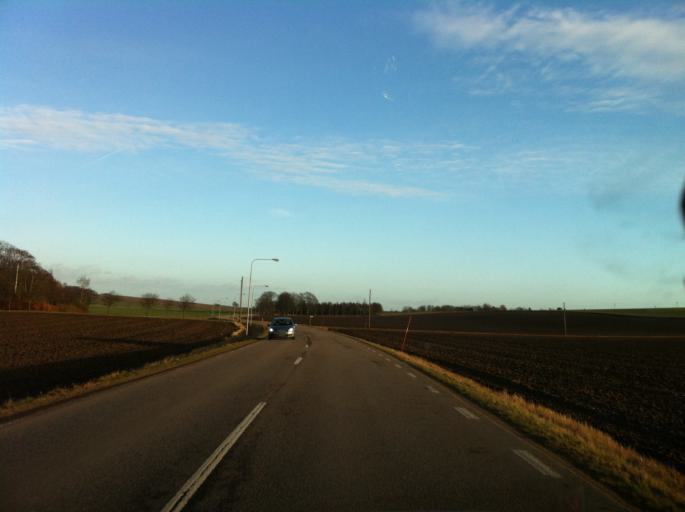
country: SE
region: Skane
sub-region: Helsingborg
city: Glumslov
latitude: 55.9376
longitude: 12.8490
